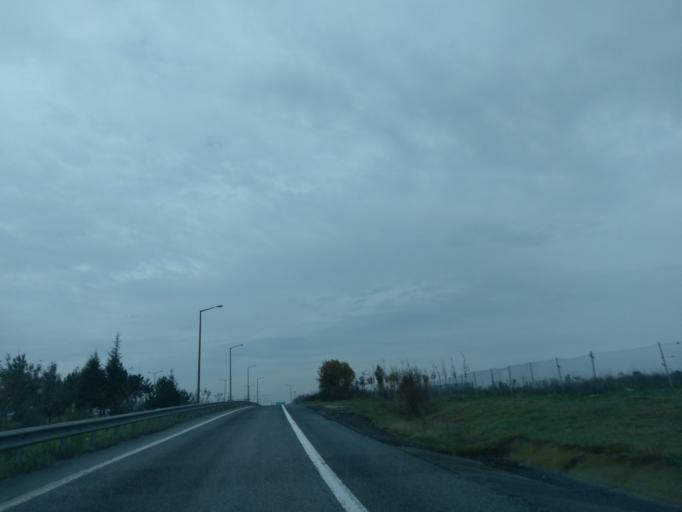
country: TR
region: Istanbul
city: Buyukcavuslu
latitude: 41.1935
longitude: 28.0859
